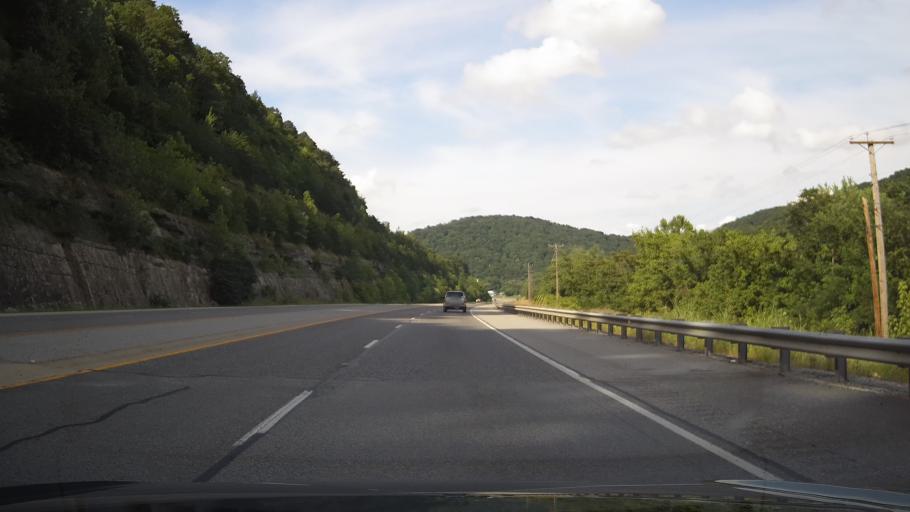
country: US
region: Kentucky
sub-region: Lawrence County
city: Louisa
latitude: 37.9873
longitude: -82.6671
